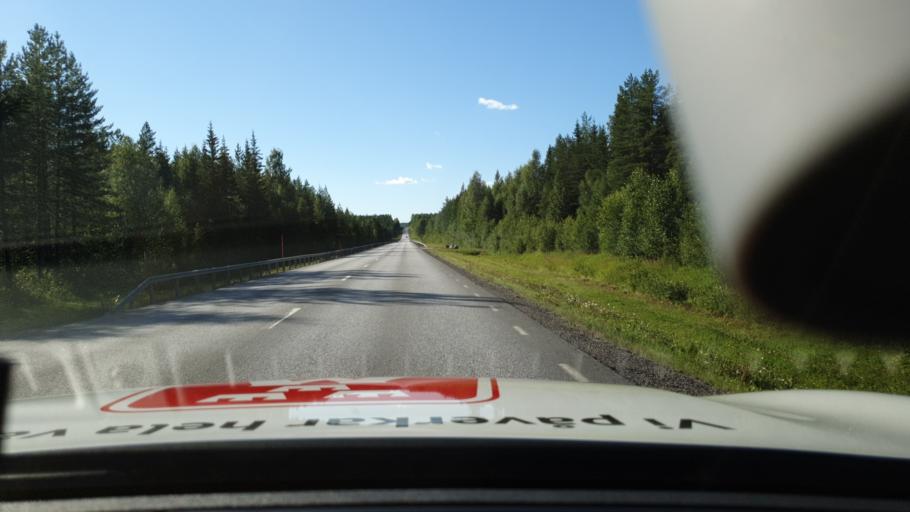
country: SE
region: Norrbotten
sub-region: Pitea Kommun
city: Norrfjarden
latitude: 65.6082
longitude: 21.4640
